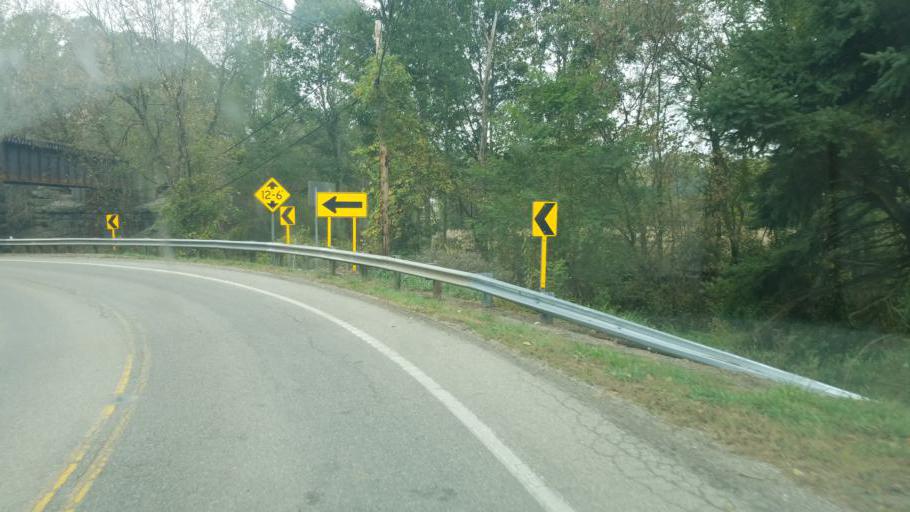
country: US
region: Ohio
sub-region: Tuscarawas County
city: Strasburg
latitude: 40.6553
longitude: -81.4653
